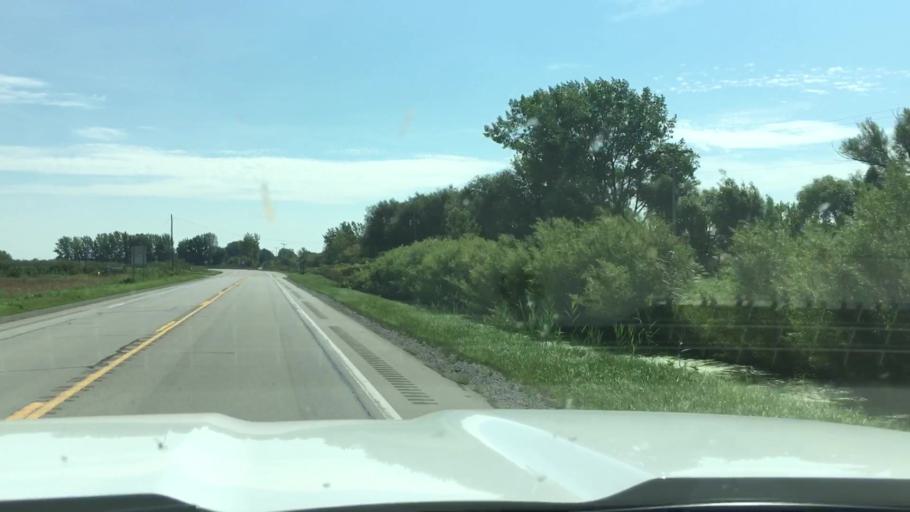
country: US
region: Michigan
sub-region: Tuscola County
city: Reese
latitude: 43.5805
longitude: -83.7014
